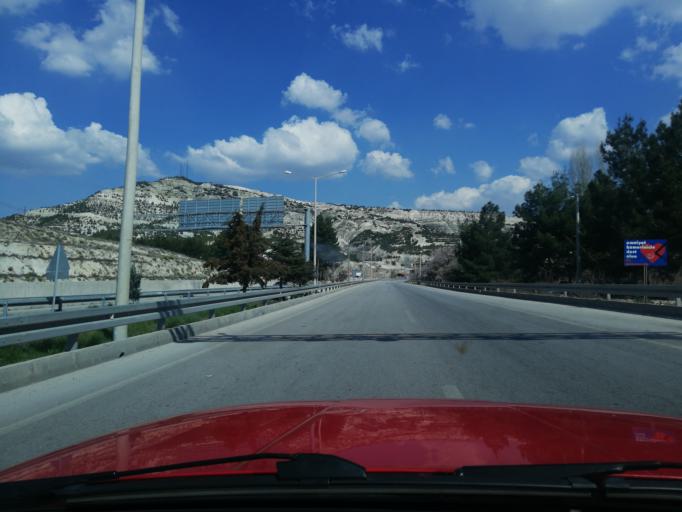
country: TR
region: Burdur
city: Burdur
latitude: 37.7088
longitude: 30.2983
